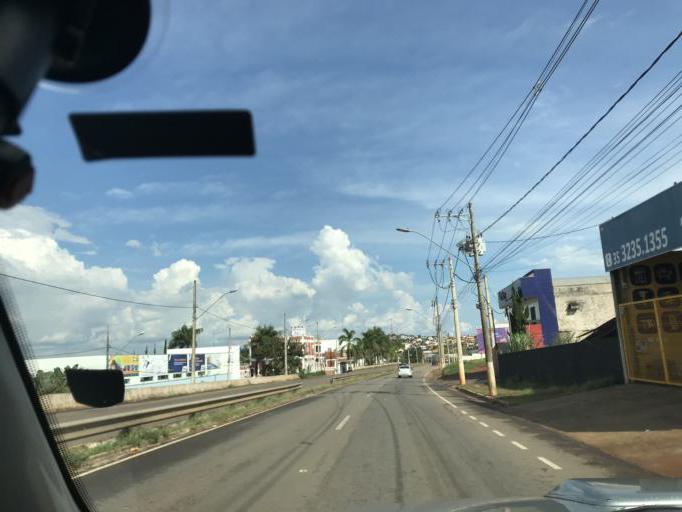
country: BR
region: Minas Gerais
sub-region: Tres Coracoes
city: Tres Coracoes
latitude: -21.6683
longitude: -45.2737
